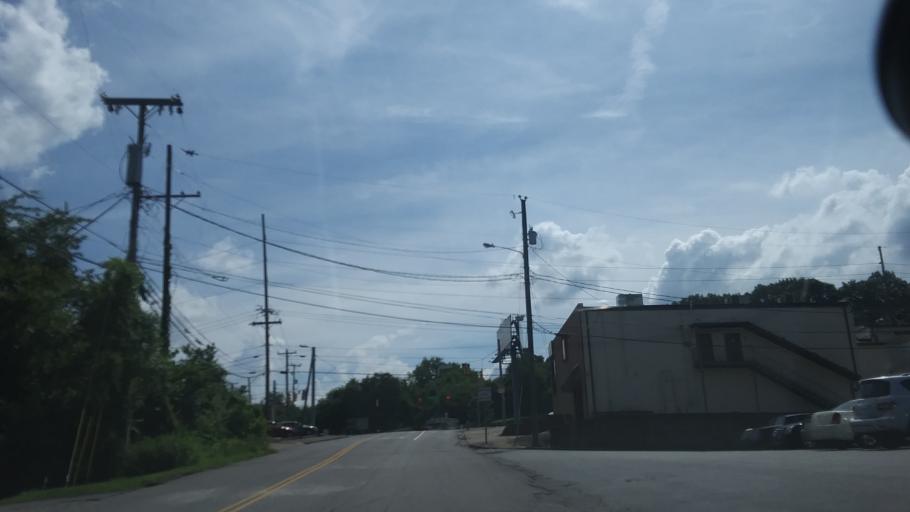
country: US
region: Tennessee
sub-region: Rutherford County
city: La Vergne
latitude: 36.0750
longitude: -86.6377
